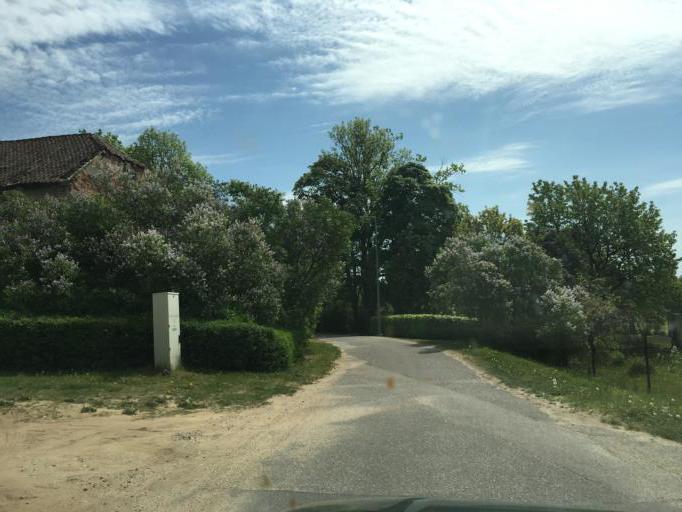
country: LV
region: Talsu Rajons
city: Valdemarpils
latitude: 57.3693
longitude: 22.5946
